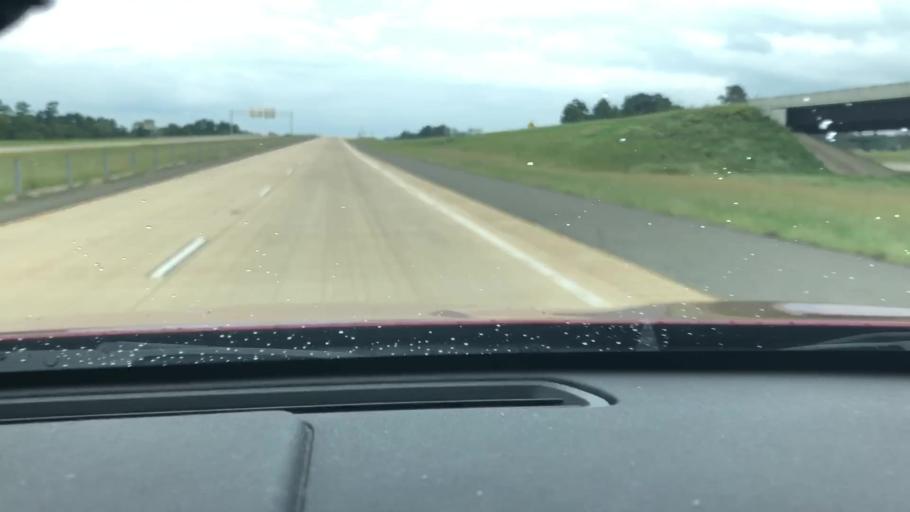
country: US
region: Texas
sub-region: Bowie County
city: Texarkana
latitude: 33.3895
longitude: -94.0167
